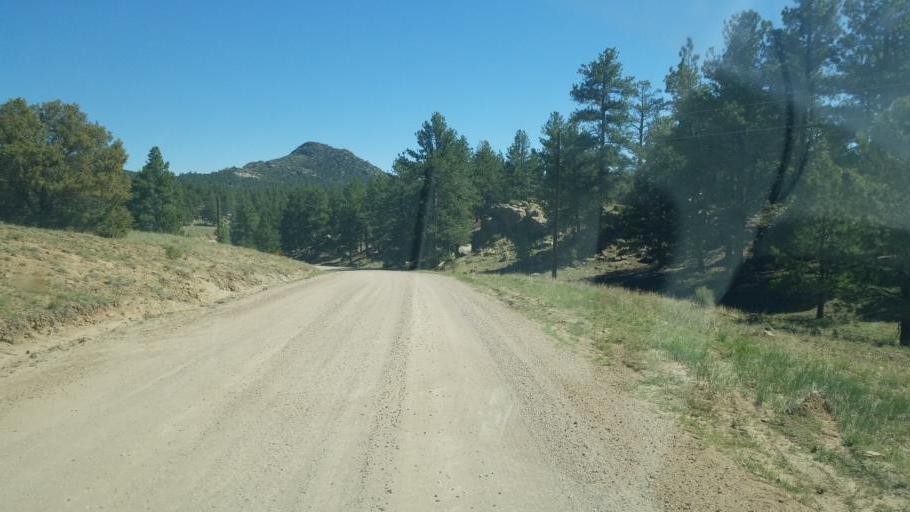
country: US
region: Colorado
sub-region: Custer County
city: Westcliffe
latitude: 38.2080
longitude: -105.4440
